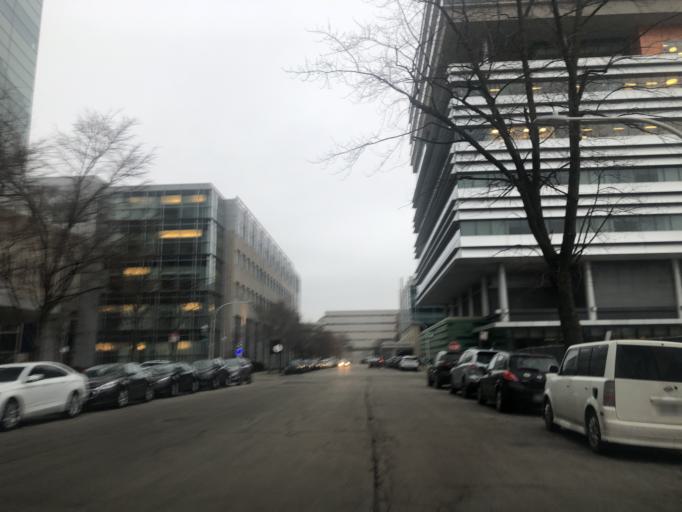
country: US
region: Illinois
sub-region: Cook County
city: Chicago
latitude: 41.7918
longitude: -87.6038
